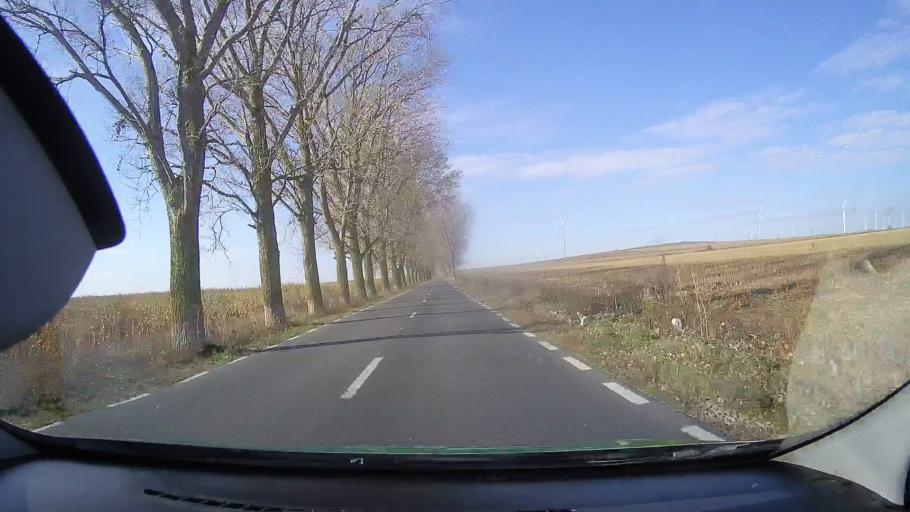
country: RO
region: Tulcea
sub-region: Comuna Valea Nucarilor
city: Iazurile
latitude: 45.0262
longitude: 28.9984
